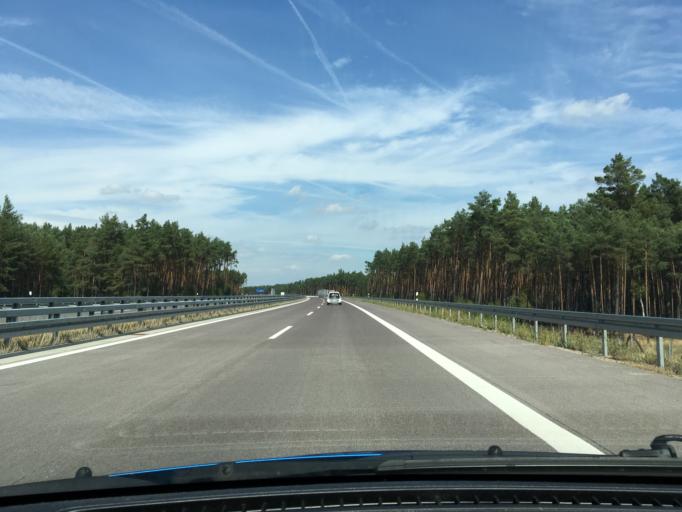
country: DE
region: Mecklenburg-Vorpommern
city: Gross Laasch
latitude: 53.3997
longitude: 11.5326
